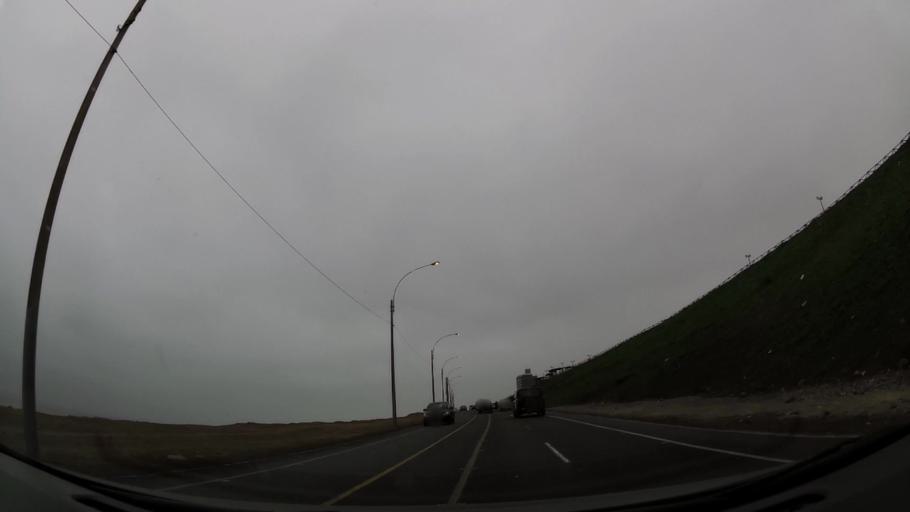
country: PE
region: Callao
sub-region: Callao
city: Callao
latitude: -12.0887
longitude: -77.0911
